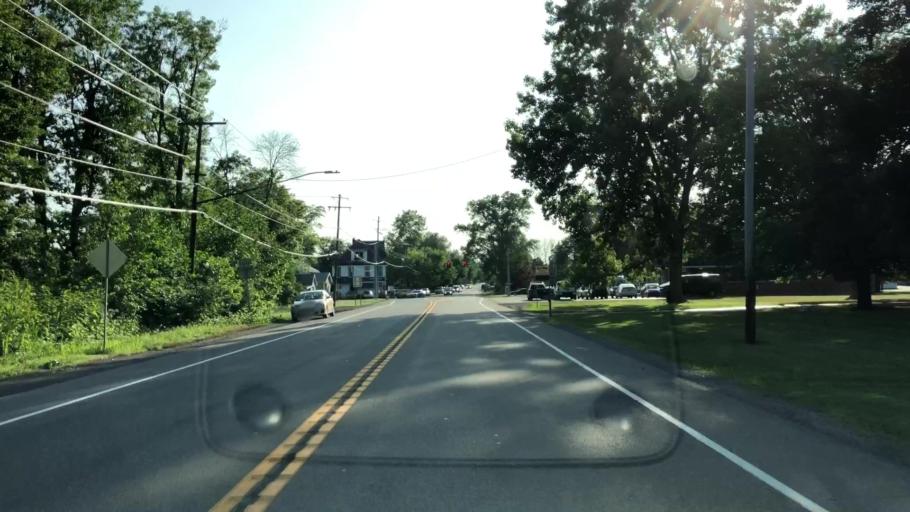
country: US
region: New York
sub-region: Erie County
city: Depew
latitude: 42.8588
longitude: -78.7073
